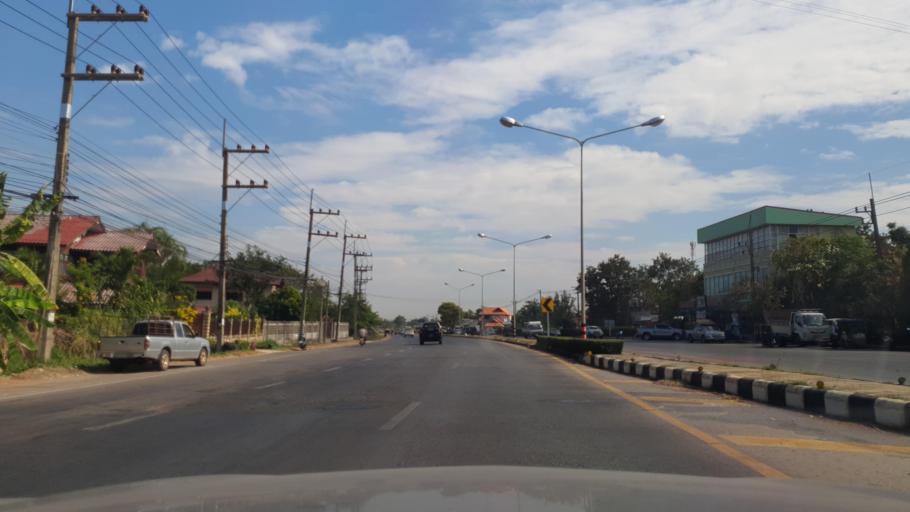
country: TH
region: Kalasin
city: Yang Talat
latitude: 16.4031
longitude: 103.4372
